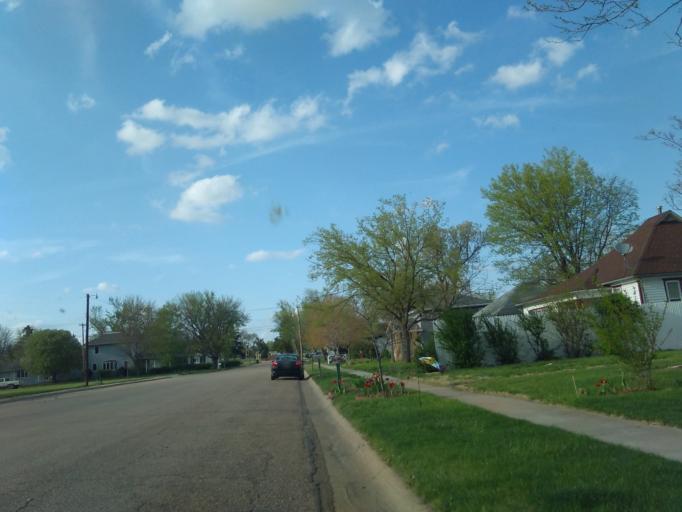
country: US
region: Nebraska
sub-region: Franklin County
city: Franklin
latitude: 40.0973
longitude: -98.9535
